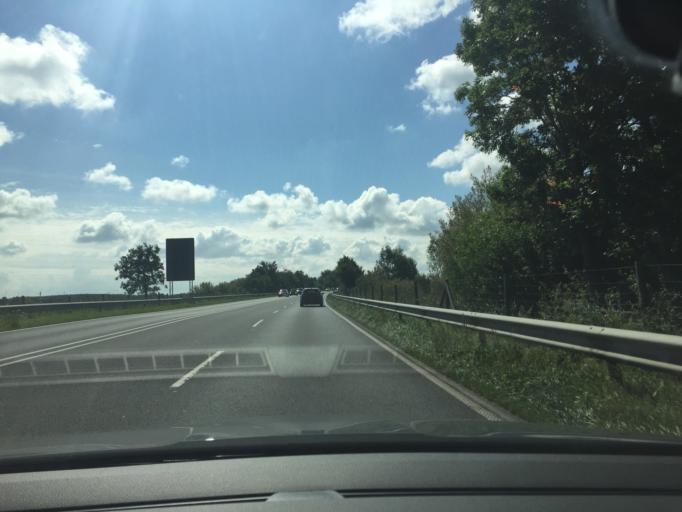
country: DE
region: Lower Saxony
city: Jever
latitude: 53.5827
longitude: 7.9218
